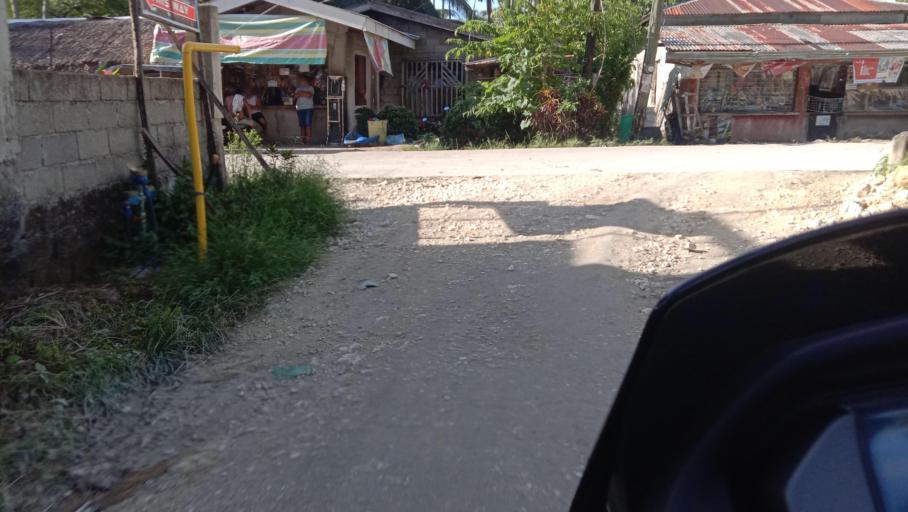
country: PH
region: Caraga
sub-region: Province of Agusan del Sur
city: Alegria
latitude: 8.4815
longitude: 125.9646
